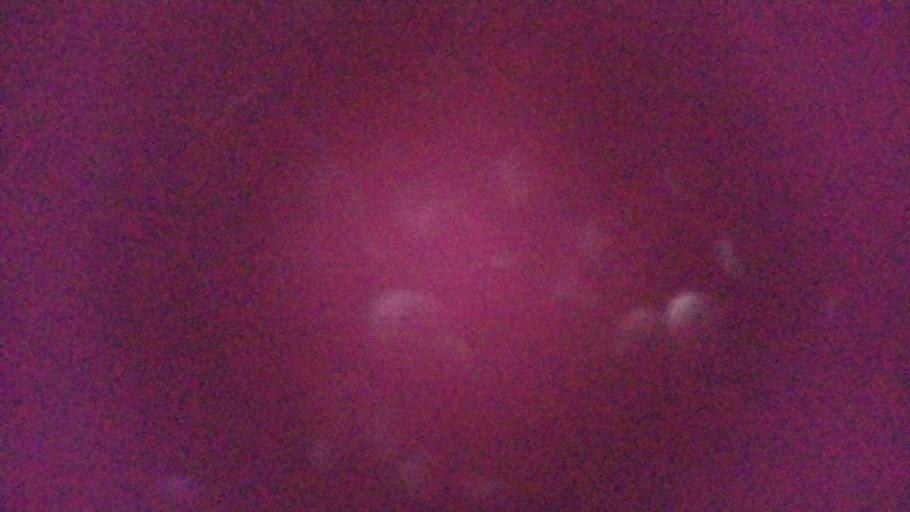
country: US
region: Florida
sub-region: Lee County
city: Olga
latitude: 26.7771
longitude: -81.7415
